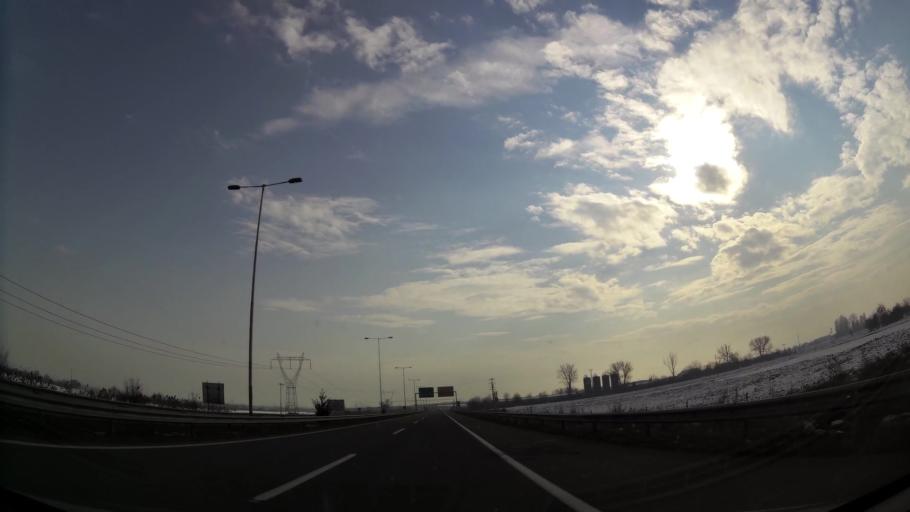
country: MK
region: Aracinovo
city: Arachinovo
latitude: 42.0230
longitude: 21.5319
